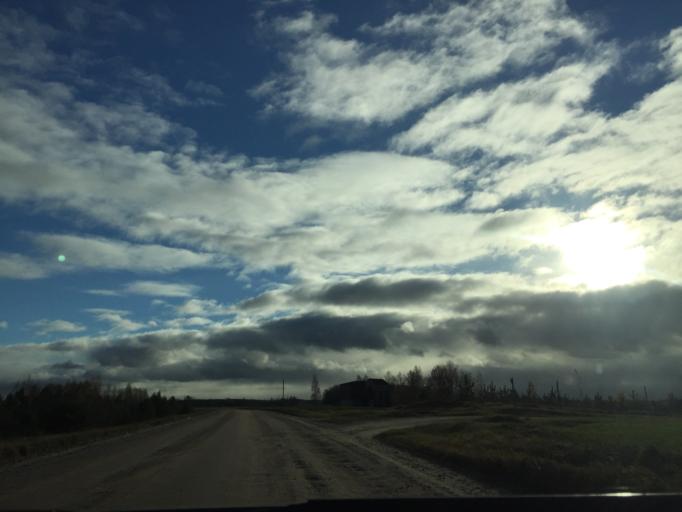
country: LV
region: Kandava
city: Kandava
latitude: 56.9676
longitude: 22.9365
